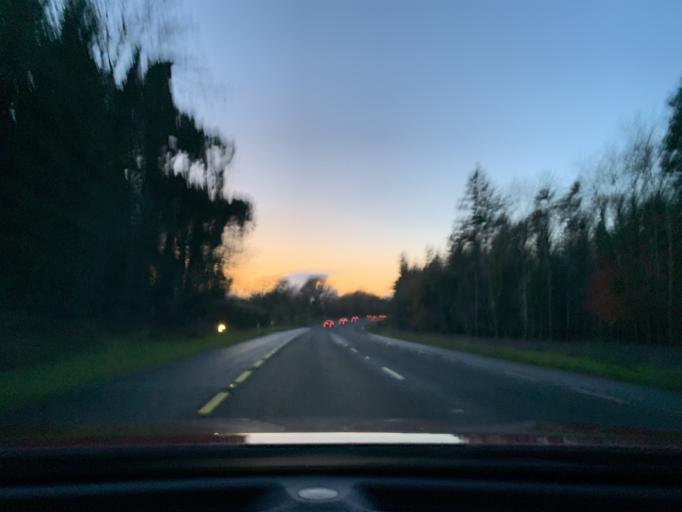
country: IE
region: Connaught
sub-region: Roscommon
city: Boyle
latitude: 53.9690
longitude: -8.2223
